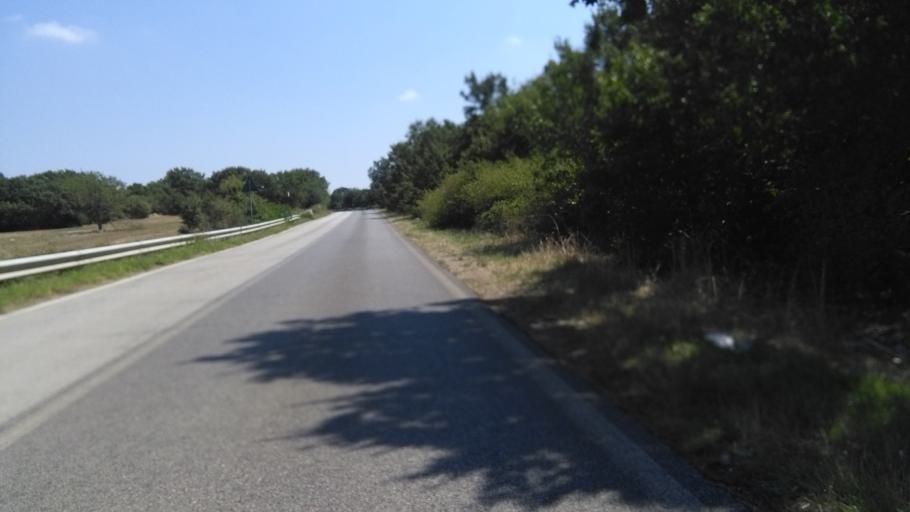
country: IT
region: Apulia
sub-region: Provincia di Bari
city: Alberobello
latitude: 40.8081
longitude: 17.1871
